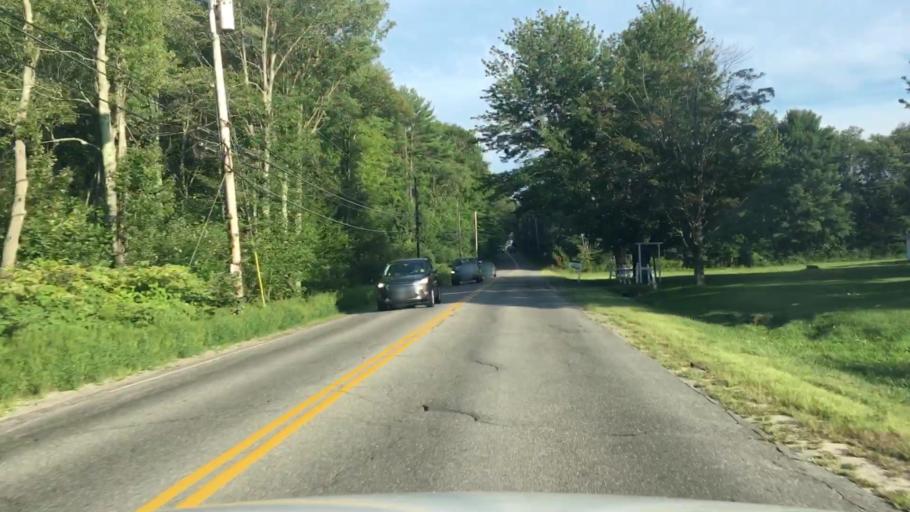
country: US
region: Maine
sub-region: Cumberland County
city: South Windham
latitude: 43.7181
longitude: -70.3951
